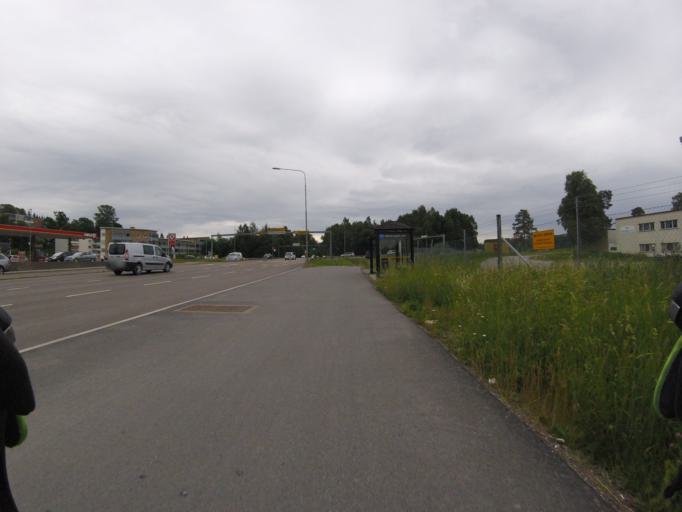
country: NO
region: Akershus
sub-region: Skedsmo
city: Lillestrom
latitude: 59.9682
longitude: 11.0514
